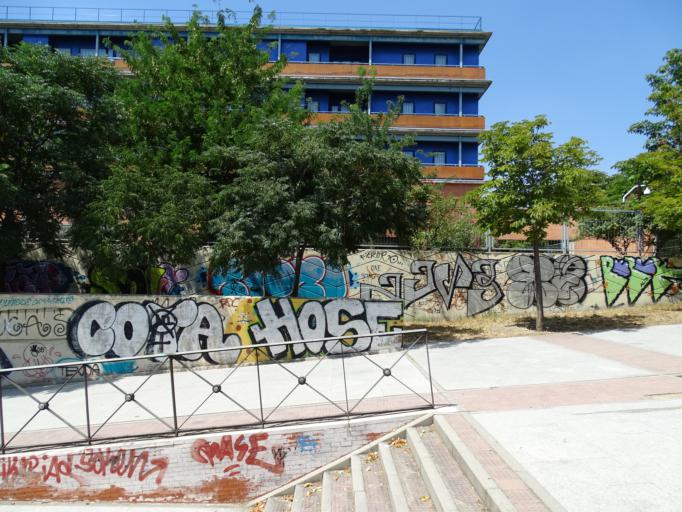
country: ES
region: Madrid
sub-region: Provincia de Madrid
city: Arganzuela
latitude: 40.4005
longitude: -3.7055
